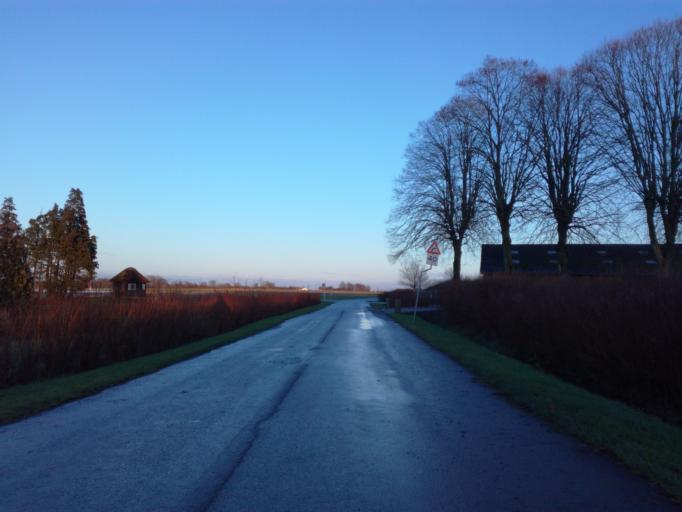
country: DK
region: South Denmark
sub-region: Fredericia Kommune
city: Taulov
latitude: 55.5540
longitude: 9.6442
